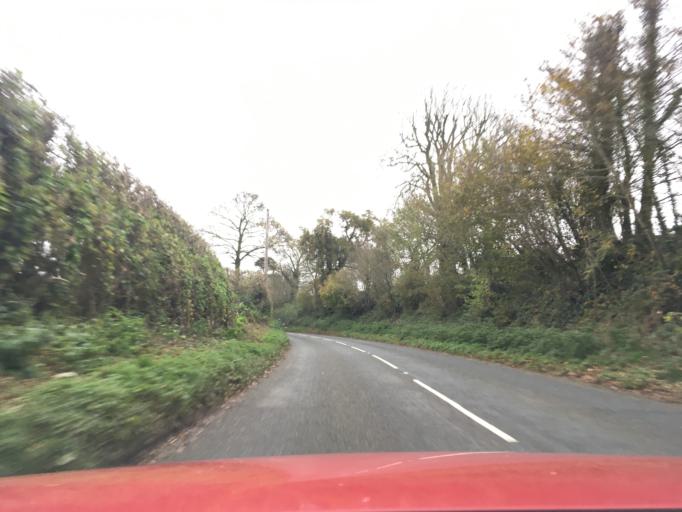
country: GB
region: England
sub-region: Dorset
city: Sherborne
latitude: 50.9635
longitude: -2.5477
